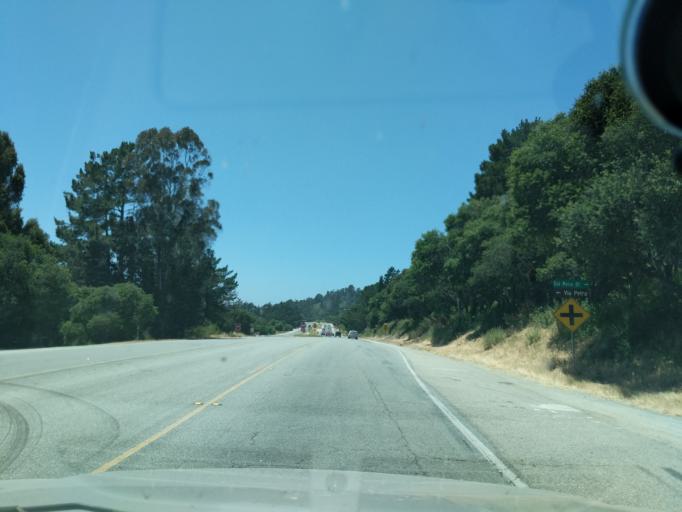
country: US
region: California
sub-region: Monterey County
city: Carmel-by-the-Sea
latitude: 36.5407
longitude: -121.8753
